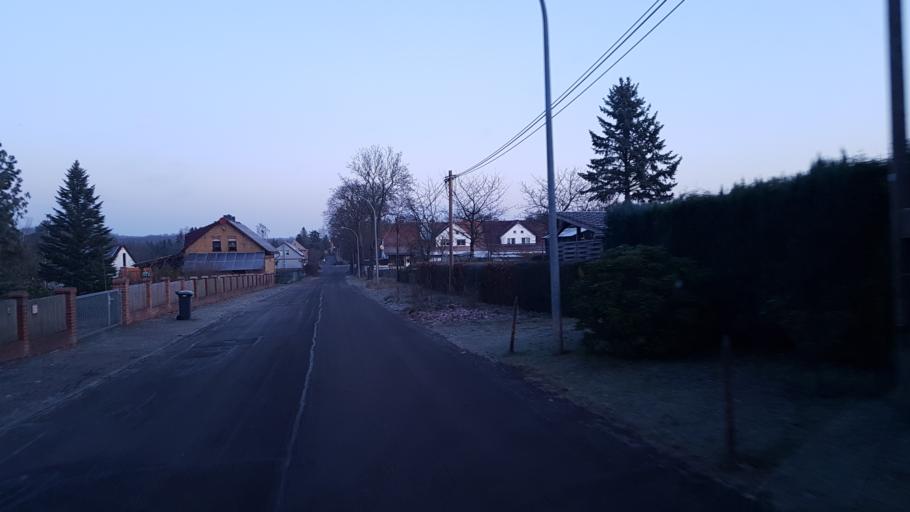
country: DE
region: Brandenburg
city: Schipkau
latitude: 51.5504
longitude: 13.8858
